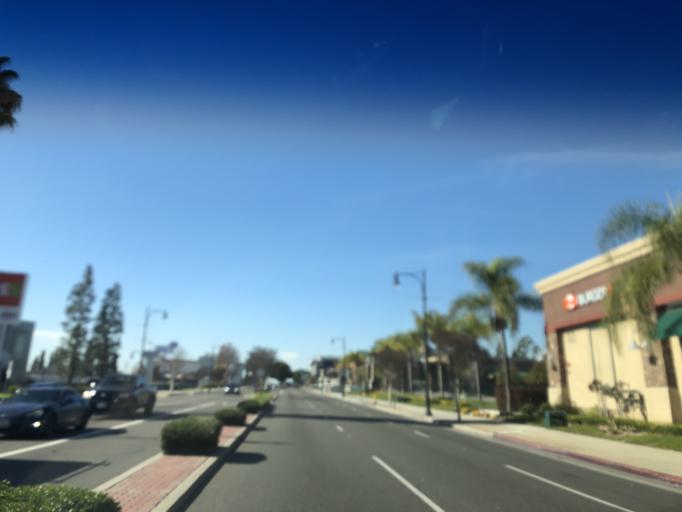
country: US
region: California
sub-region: Los Angeles County
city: East La Mirada
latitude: 33.9471
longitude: -118.0009
